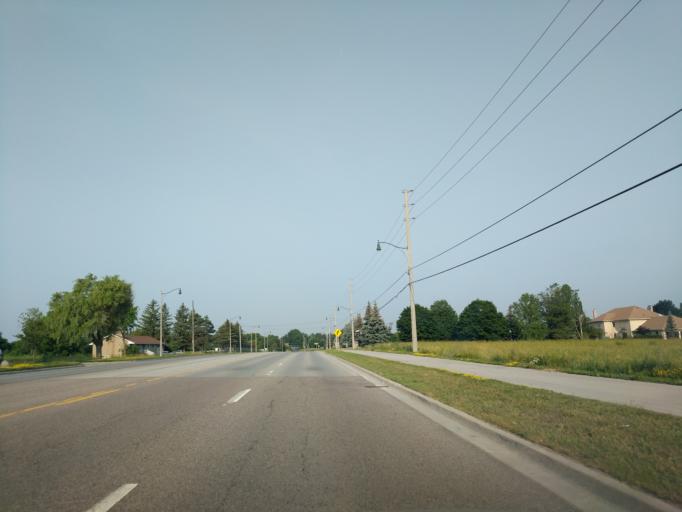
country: CA
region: Ontario
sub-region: York
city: Richmond Hill
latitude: 43.8943
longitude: -79.4145
